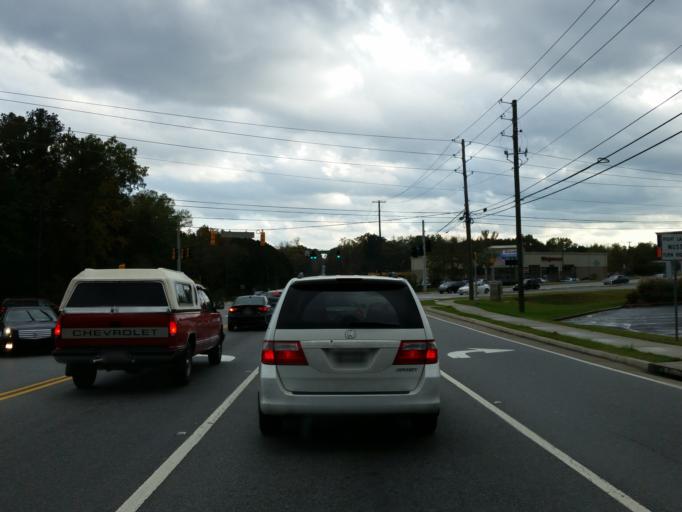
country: US
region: Georgia
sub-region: Henry County
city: Stockbridge
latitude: 33.5014
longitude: -84.2452
